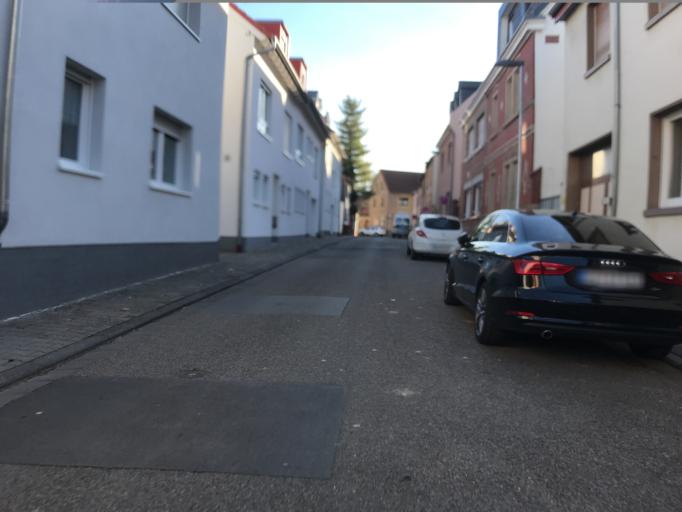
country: DE
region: Rheinland-Pfalz
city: Mainz
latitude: 49.9605
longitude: 8.2769
